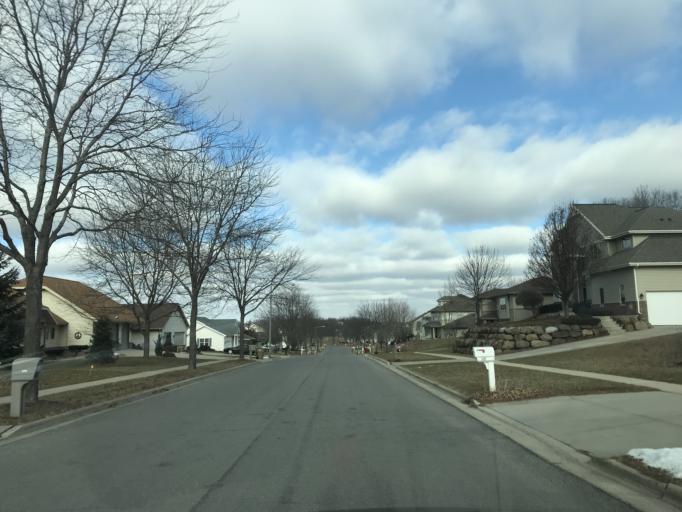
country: US
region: Wisconsin
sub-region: Dane County
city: Monona
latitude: 43.1096
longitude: -89.2913
